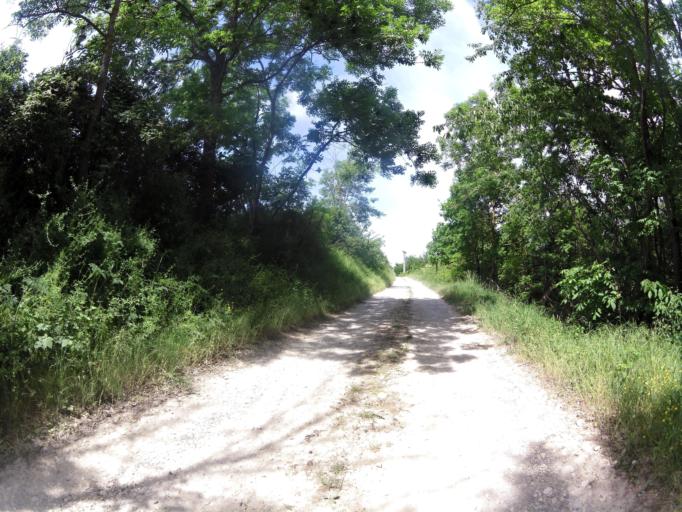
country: DE
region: Bavaria
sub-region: Regierungsbezirk Unterfranken
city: Ochsenfurt
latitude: 49.6712
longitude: 10.0331
